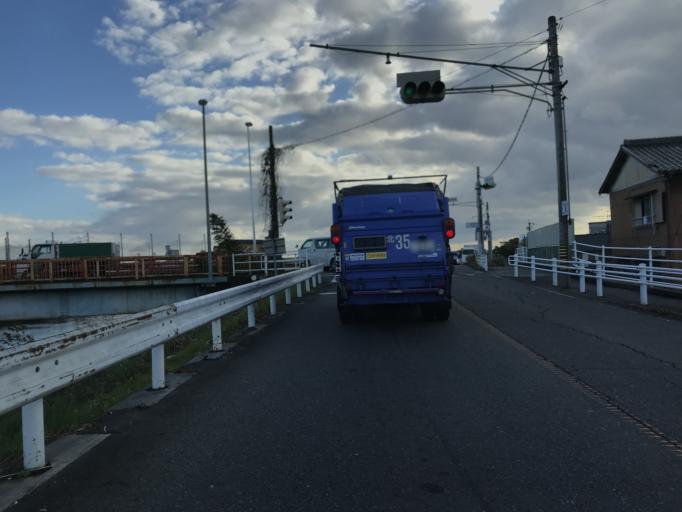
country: JP
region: Aichi
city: Nagoya-shi
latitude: 35.1863
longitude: 136.8445
